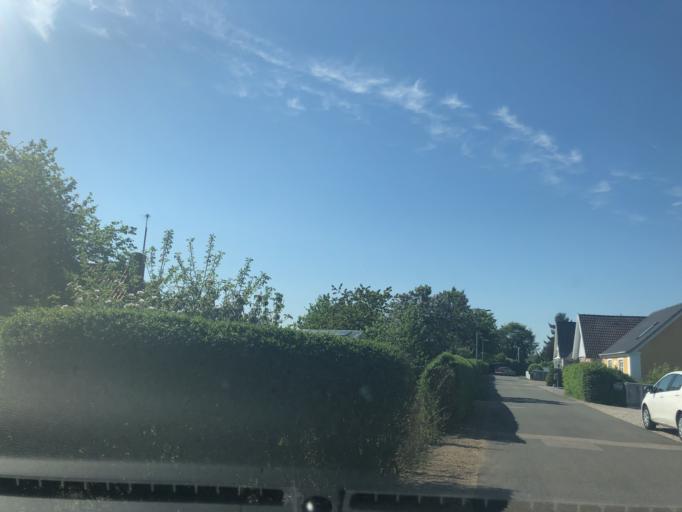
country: DK
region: Zealand
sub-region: Ringsted Kommune
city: Ringsted
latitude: 55.4569
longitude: 11.7972
